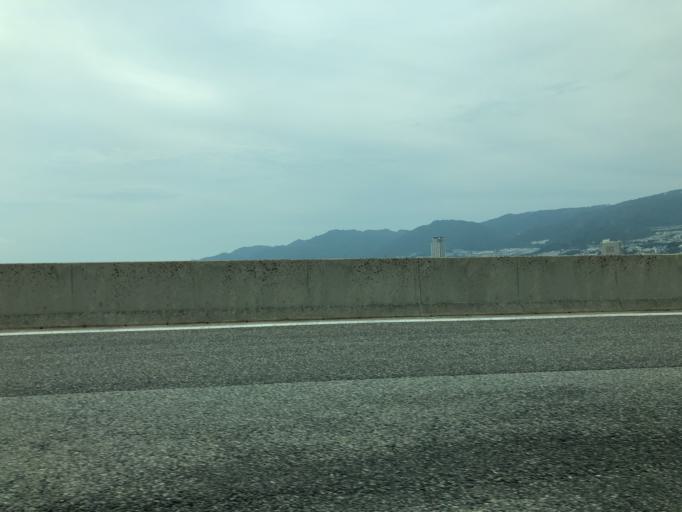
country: JP
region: Hyogo
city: Ashiya
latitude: 34.7051
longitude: 135.2741
